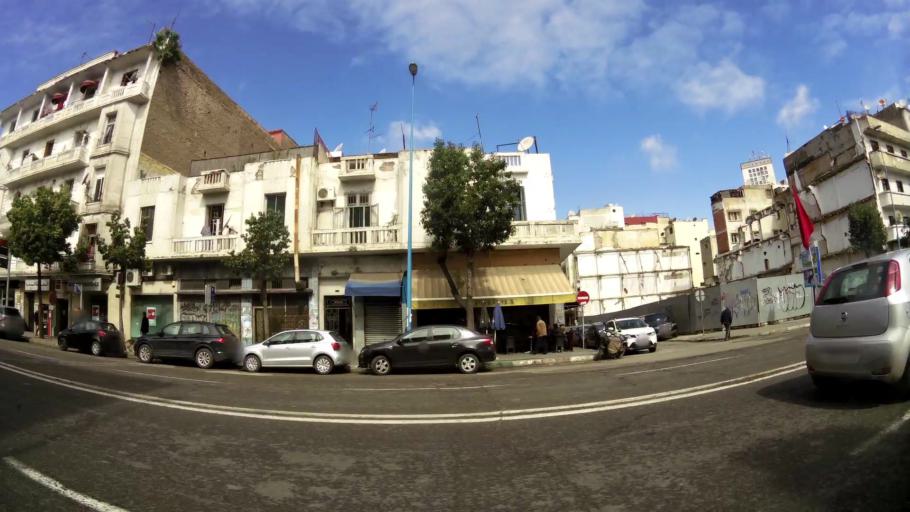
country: MA
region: Grand Casablanca
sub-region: Casablanca
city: Casablanca
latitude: 33.5833
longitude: -7.6321
